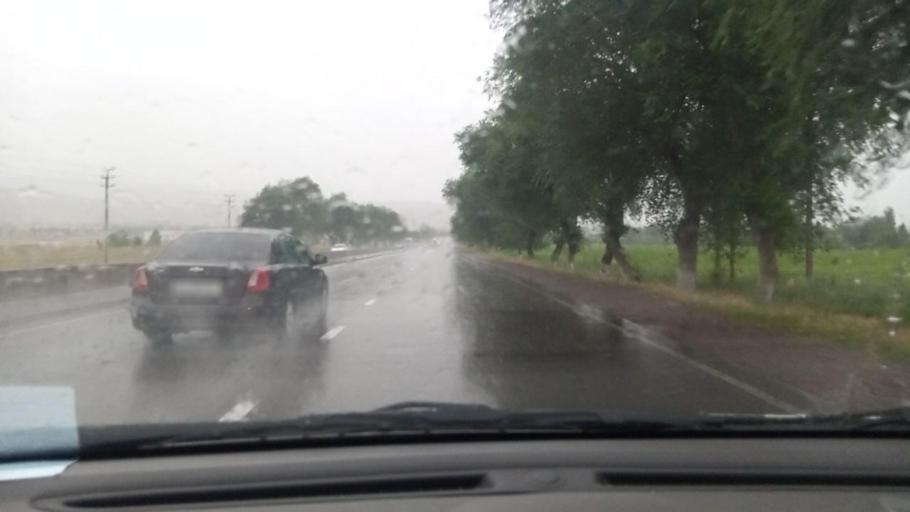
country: UZ
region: Toshkent
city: Ohangaron
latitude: 40.9199
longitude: 69.8362
